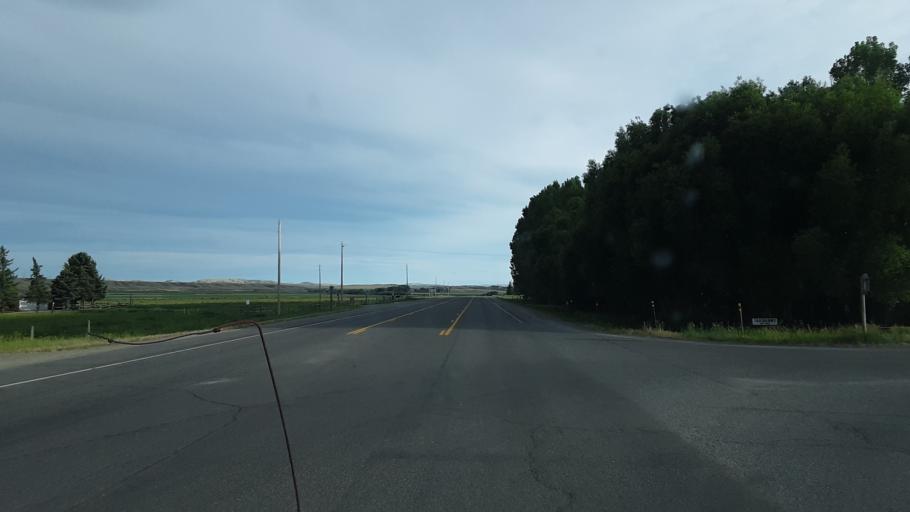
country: US
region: Wyoming
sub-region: Park County
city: Cody
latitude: 44.5883
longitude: -108.9681
